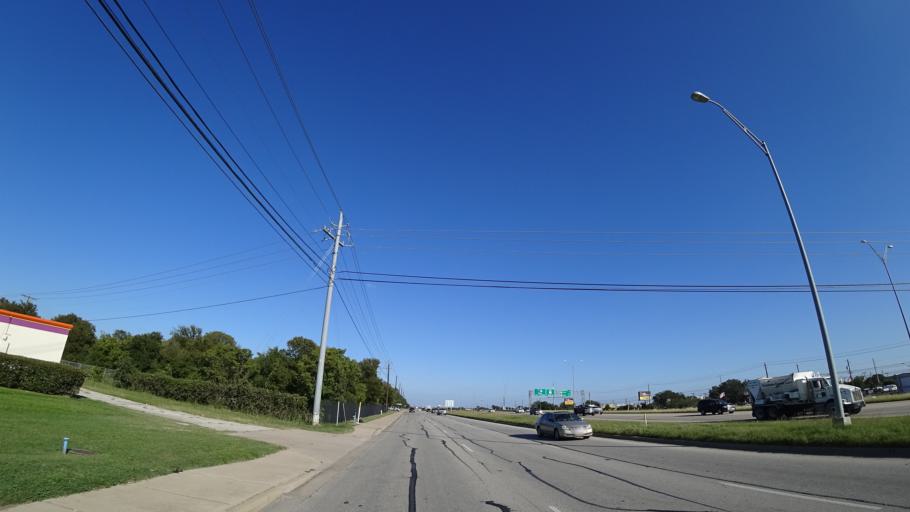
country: US
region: Texas
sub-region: Travis County
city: Austin
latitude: 30.2144
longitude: -97.7262
